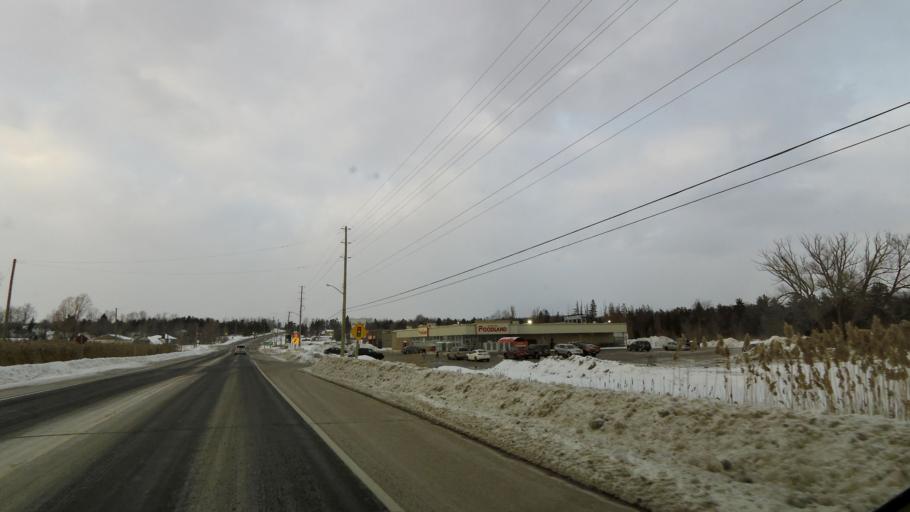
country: CA
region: Ontario
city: Omemee
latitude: 44.6612
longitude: -78.8006
